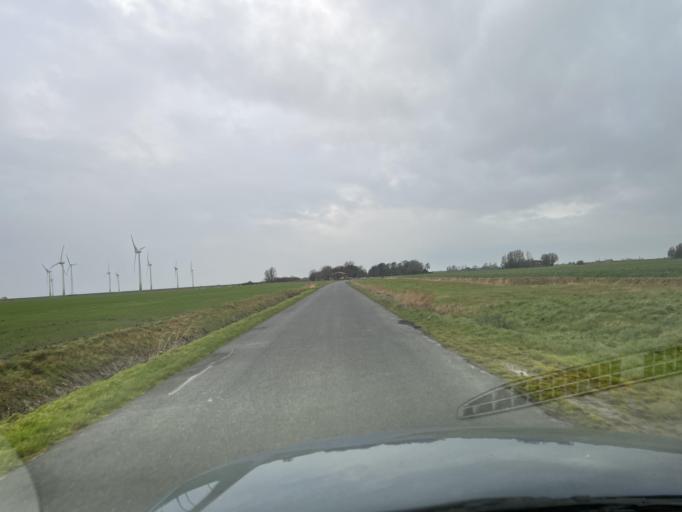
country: DE
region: Schleswig-Holstein
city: Hillgroven
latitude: 54.2156
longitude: 8.8839
